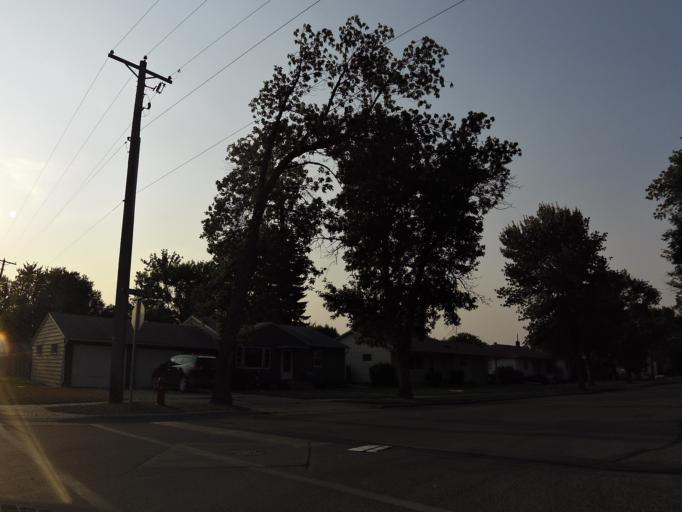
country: US
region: North Dakota
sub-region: Traill County
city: Mayville
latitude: 47.4981
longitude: -97.3159
